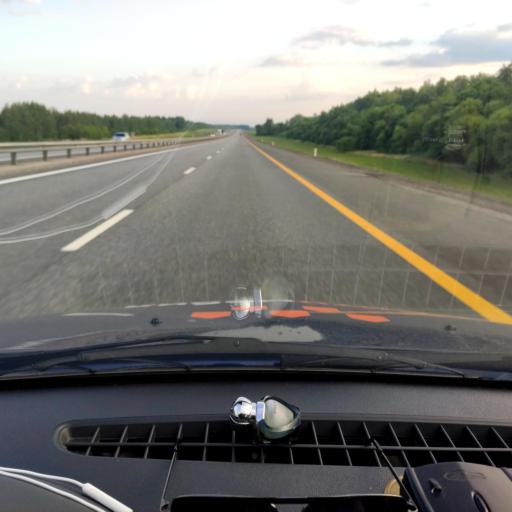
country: RU
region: Lipetsk
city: Zadonsk
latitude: 52.4760
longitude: 38.7645
